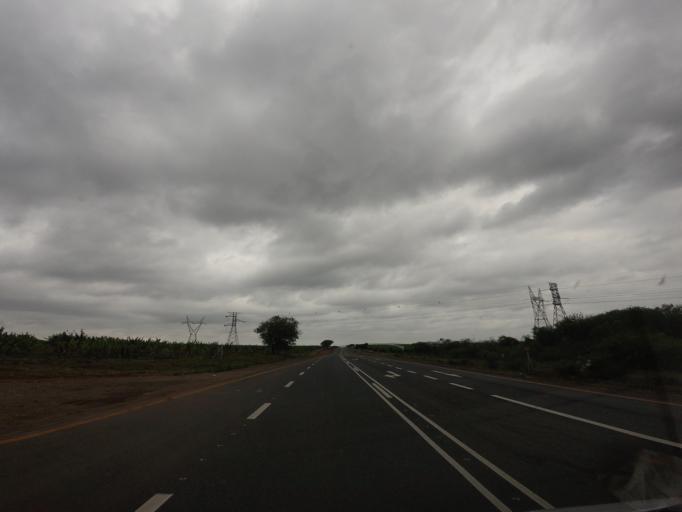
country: ZA
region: Mpumalanga
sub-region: Ehlanzeni District
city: Komatipoort
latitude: -25.4355
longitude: 31.8225
